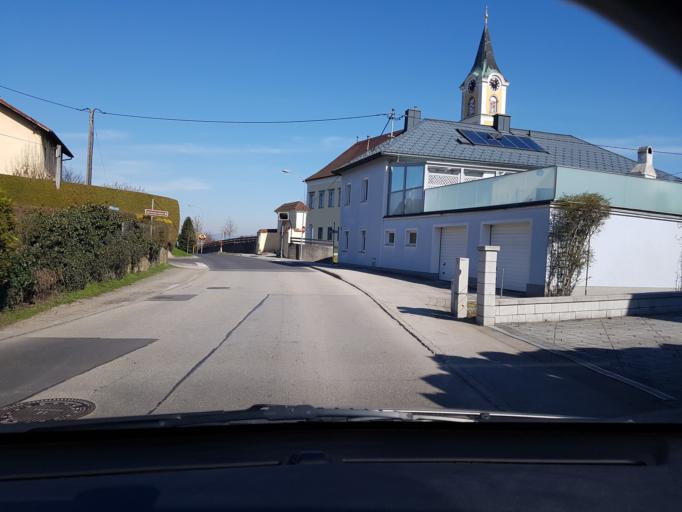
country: AT
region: Upper Austria
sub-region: Politischer Bezirk Linz-Land
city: Ansfelden
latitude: 48.2085
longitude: 14.2903
